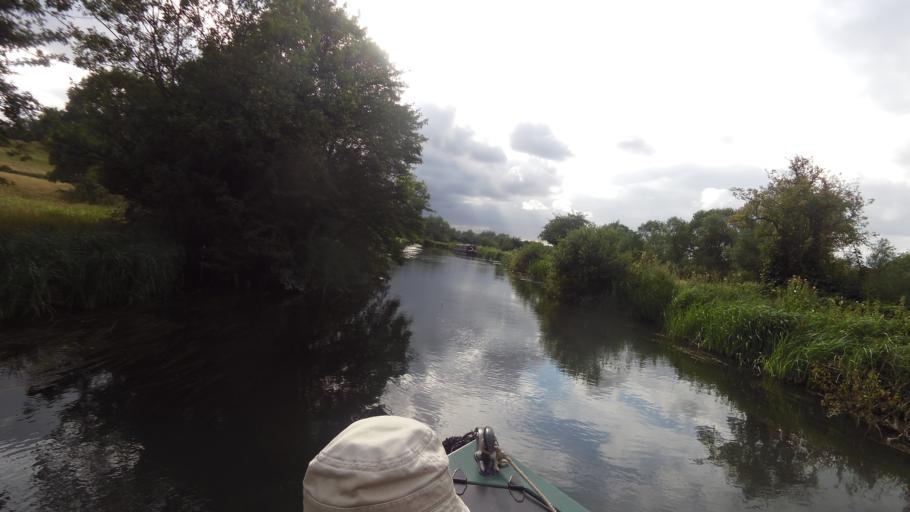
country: GB
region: England
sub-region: West Berkshire
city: Kintbury
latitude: 51.4010
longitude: -1.3972
